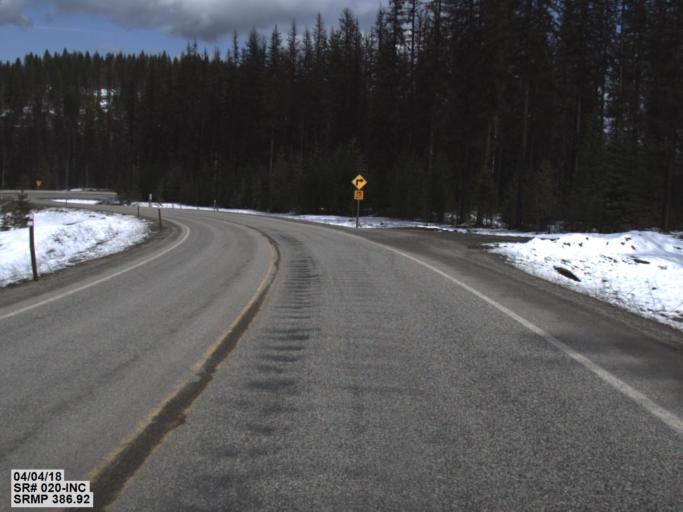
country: CA
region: British Columbia
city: Fruitvale
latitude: 48.6822
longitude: -117.4525
